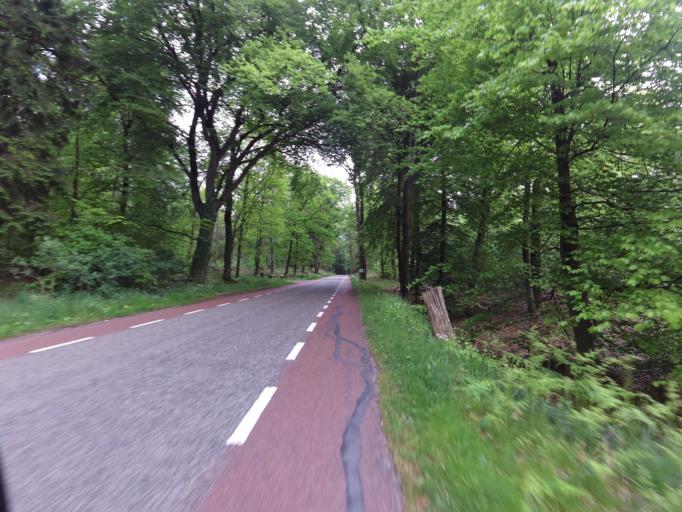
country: NL
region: Gelderland
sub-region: Gemeente Montferland
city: s-Heerenberg
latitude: 51.9000
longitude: 6.2059
